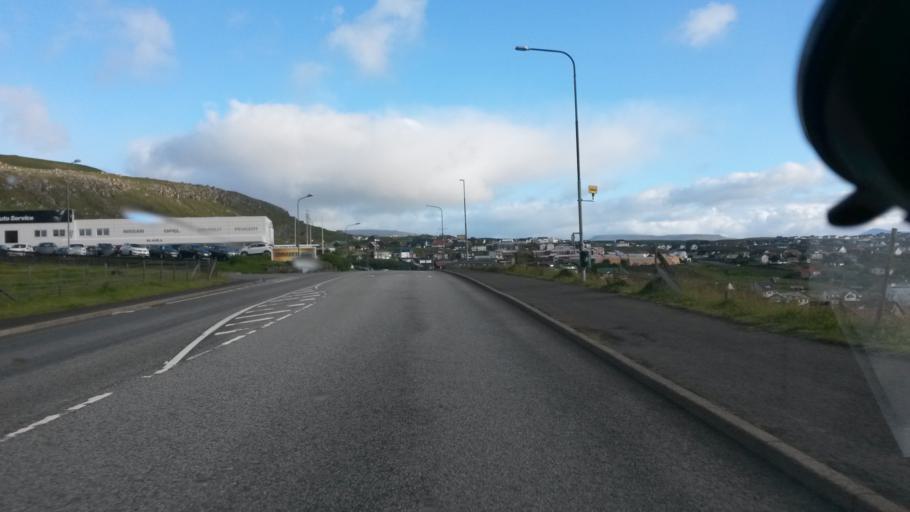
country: FO
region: Streymoy
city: Hoyvik
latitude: 62.0184
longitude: -6.7888
